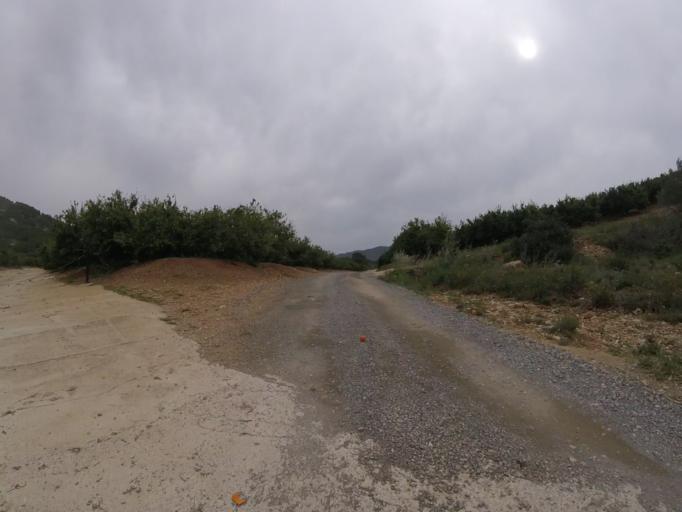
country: ES
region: Valencia
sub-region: Provincia de Castello
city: Alcala de Xivert
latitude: 40.2933
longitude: 0.2528
